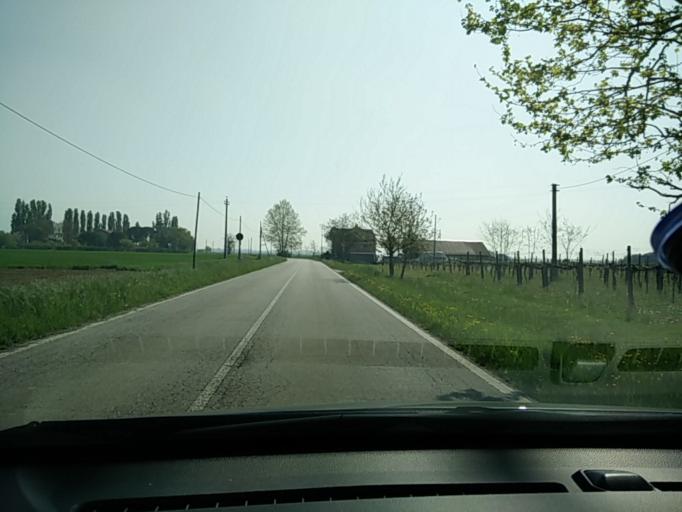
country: IT
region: Veneto
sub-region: Provincia di Treviso
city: Fornaci
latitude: 45.6697
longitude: 12.4542
